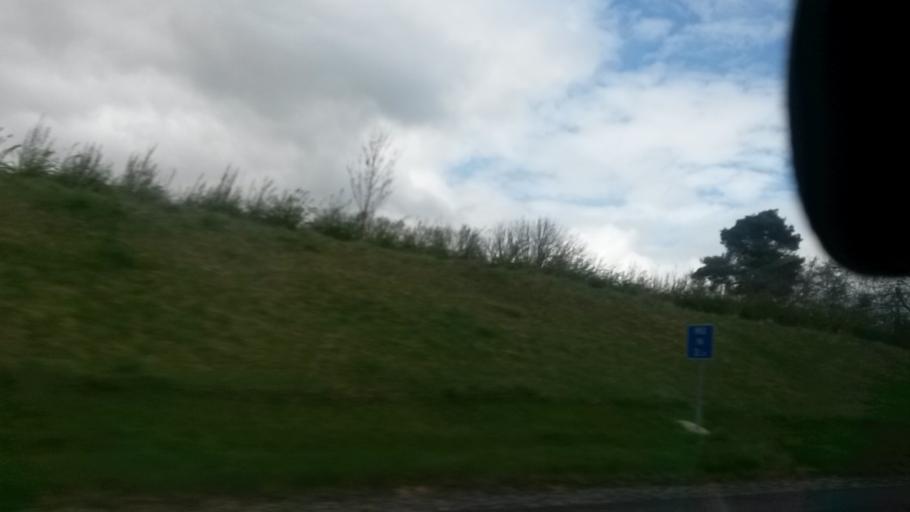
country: IE
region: Leinster
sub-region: Laois
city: Mountrath
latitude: 52.8999
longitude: -7.4896
